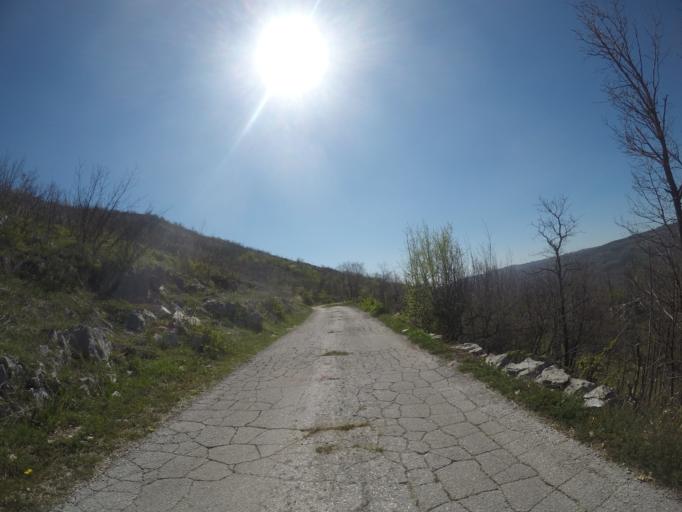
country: ME
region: Danilovgrad
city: Danilovgrad
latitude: 42.5370
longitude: 19.0141
